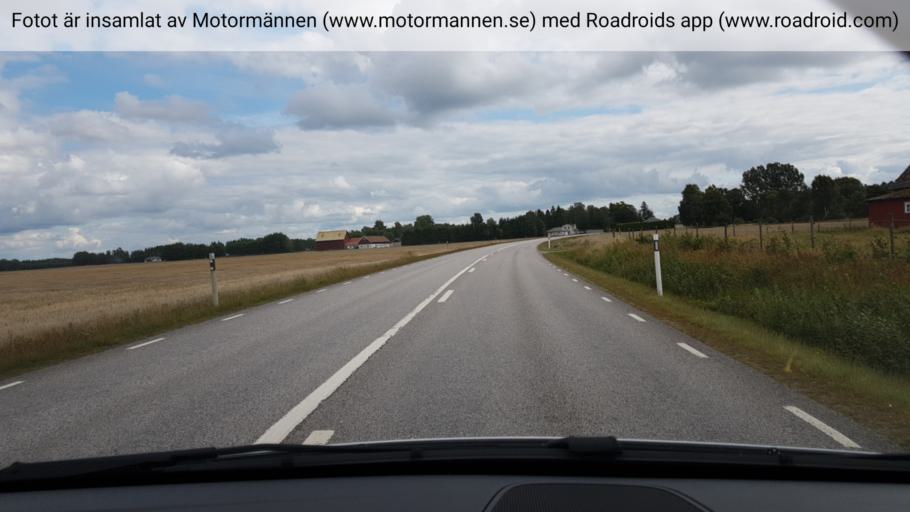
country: SE
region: Vaestra Goetaland
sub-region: Vara Kommun
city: Kvanum
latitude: 58.2239
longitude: 13.1834
